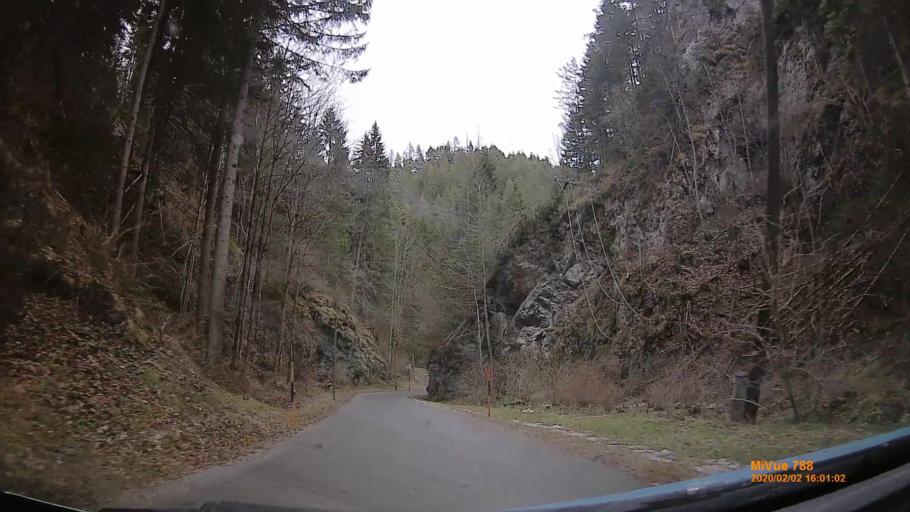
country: AT
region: Lower Austria
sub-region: Politischer Bezirk Neunkirchen
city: Semmering
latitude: 47.6582
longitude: 15.8003
